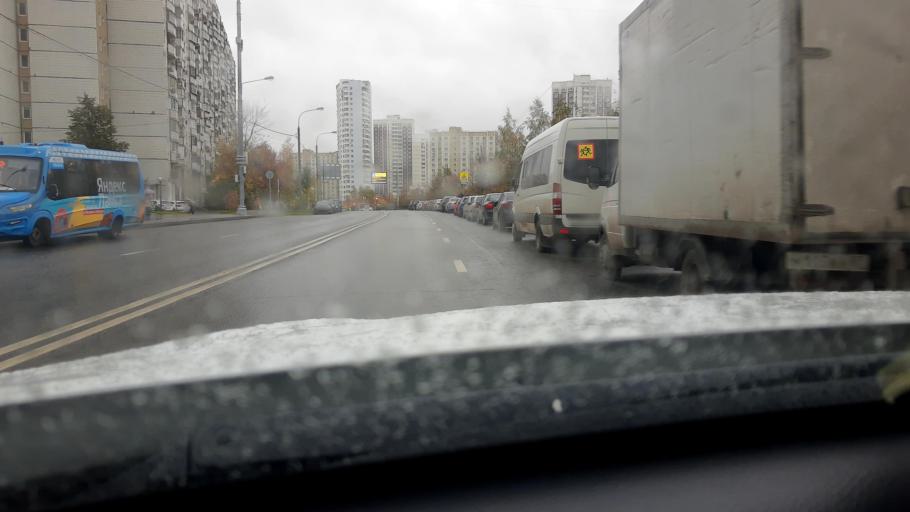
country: RU
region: Moskovskaya
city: Pavshino
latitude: 55.8521
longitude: 37.3537
